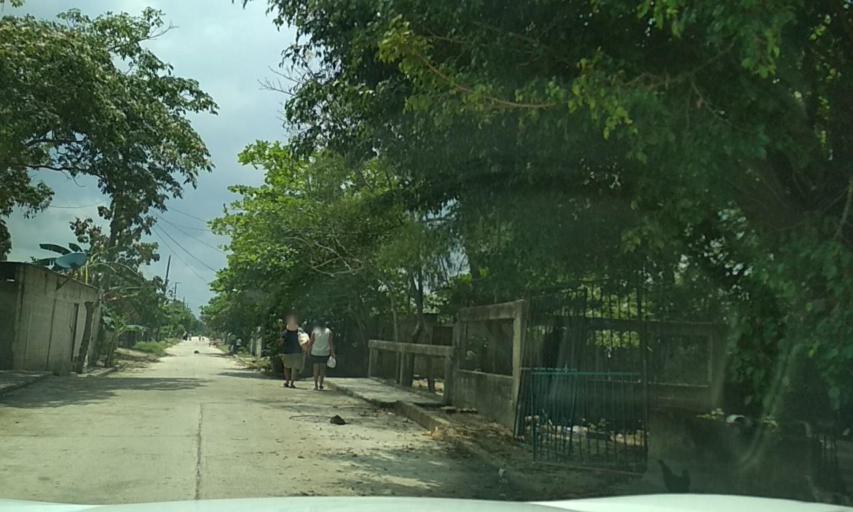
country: MX
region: Veracruz
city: Las Choapas
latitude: 17.8928
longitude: -94.0973
